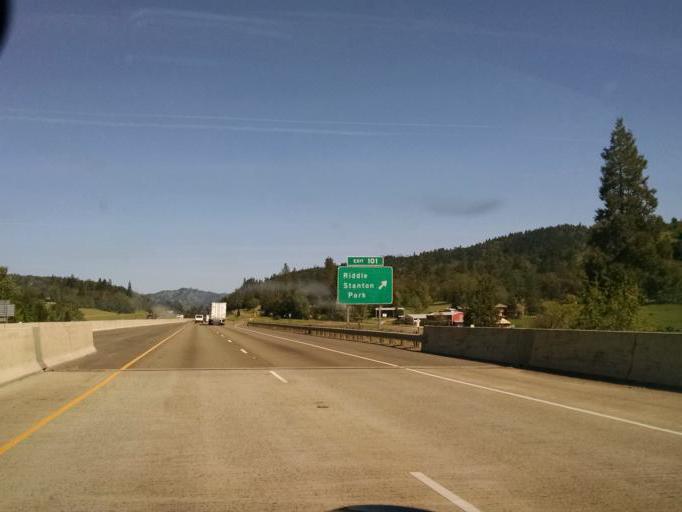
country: US
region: Oregon
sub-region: Douglas County
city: Tri-City
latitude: 42.9478
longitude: -123.3228
